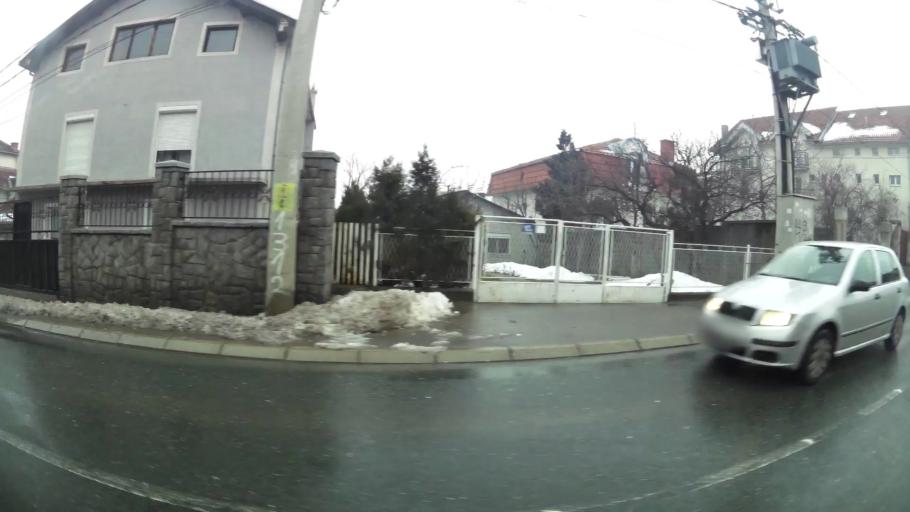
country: RS
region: Central Serbia
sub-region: Belgrade
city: Zvezdara
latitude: 44.7687
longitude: 20.5131
